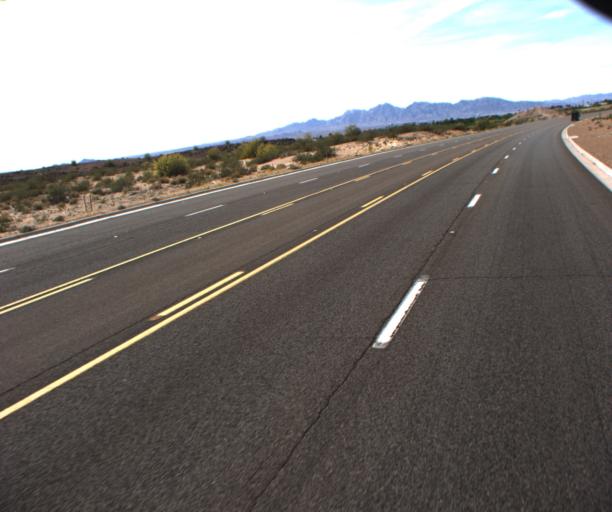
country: US
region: Arizona
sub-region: Mohave County
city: Lake Havasu City
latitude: 34.4559
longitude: -114.3281
